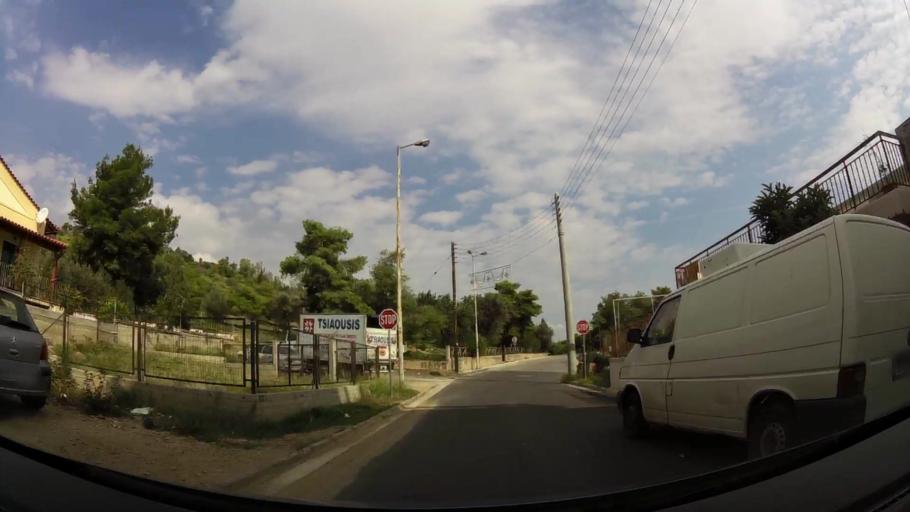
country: GR
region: Attica
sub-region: Nomarchia Athinas
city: Petroupolis
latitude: 38.0484
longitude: 23.6899
